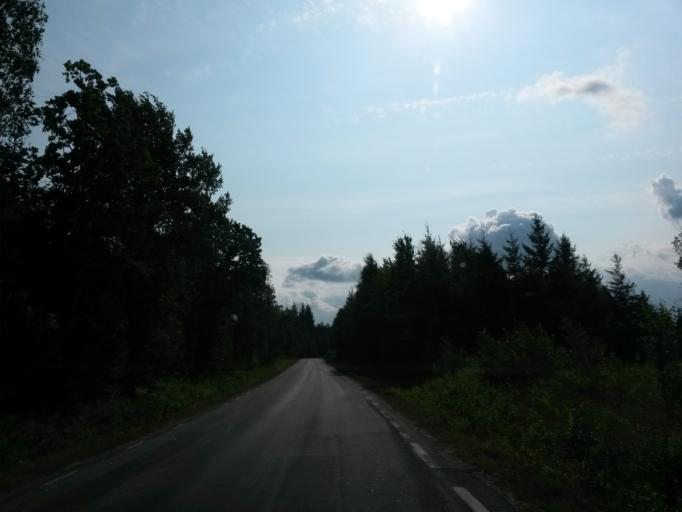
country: SE
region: Vaestra Goetaland
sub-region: Vargarda Kommun
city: Jonstorp
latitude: 58.0115
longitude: 12.6659
